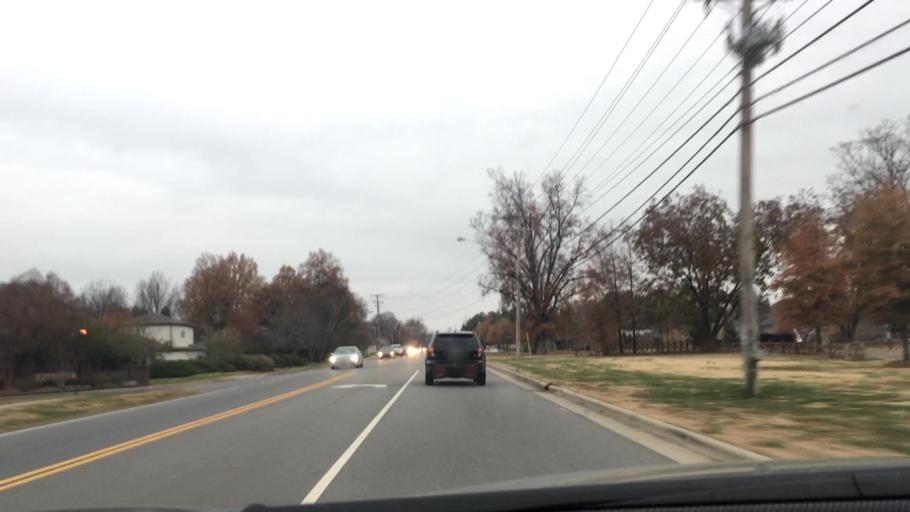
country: US
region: North Carolina
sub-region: Mecklenburg County
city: Cornelius
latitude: 35.4565
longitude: -80.8885
